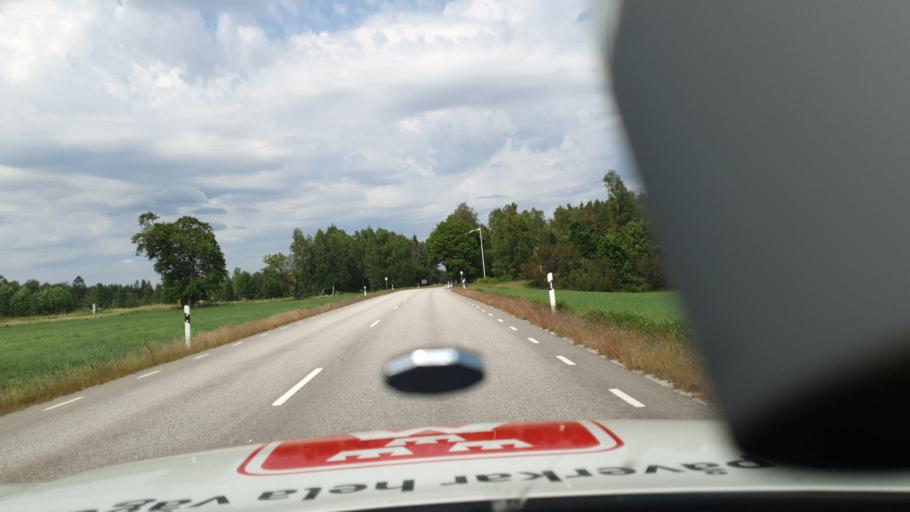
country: SE
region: Joenkoeping
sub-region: Varnamo Kommun
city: Varnamo
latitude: 57.2191
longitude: 14.0406
